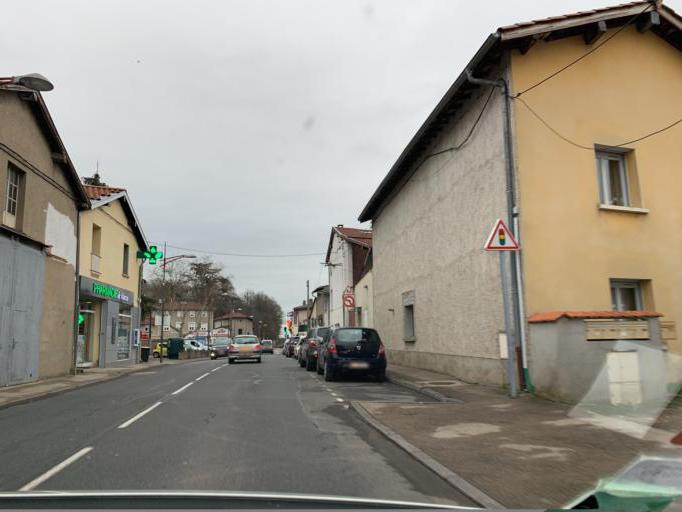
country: FR
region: Rhone-Alpes
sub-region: Departement du Rhone
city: Rillieux-la-Pape
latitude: 45.8336
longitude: 4.9115
